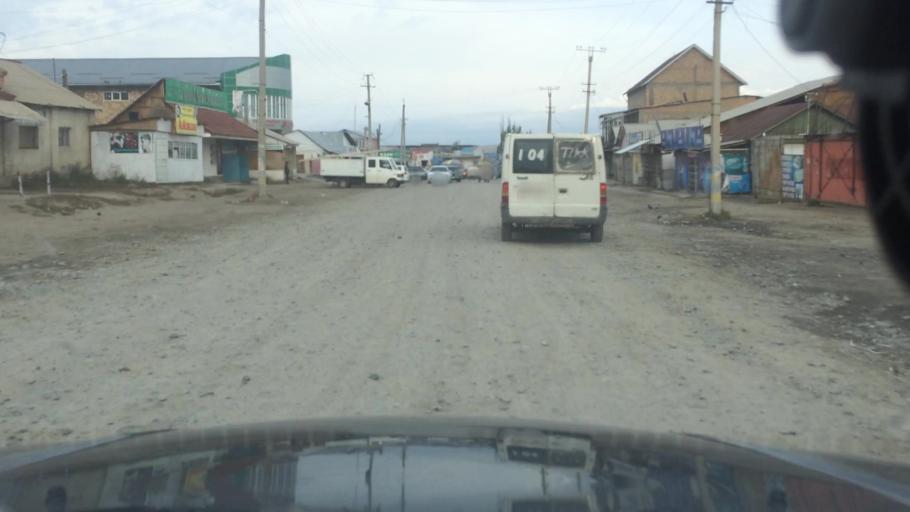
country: KG
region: Ysyk-Koel
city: Karakol
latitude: 42.4914
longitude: 78.3865
